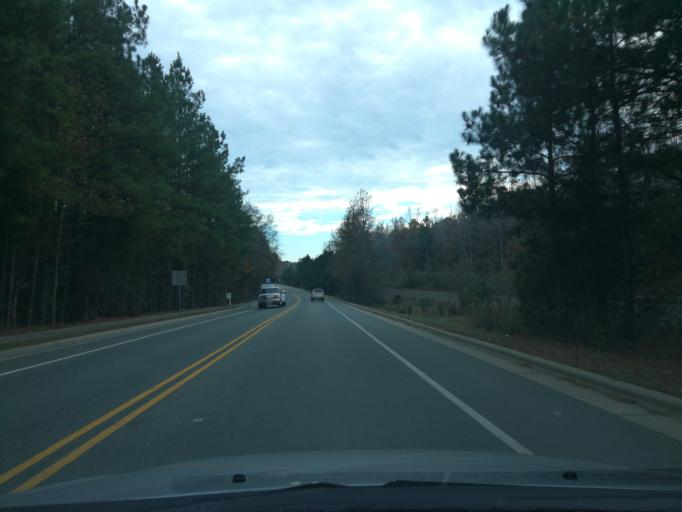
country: US
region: North Carolina
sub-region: Orange County
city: Carrboro
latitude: 35.9754
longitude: -79.0762
